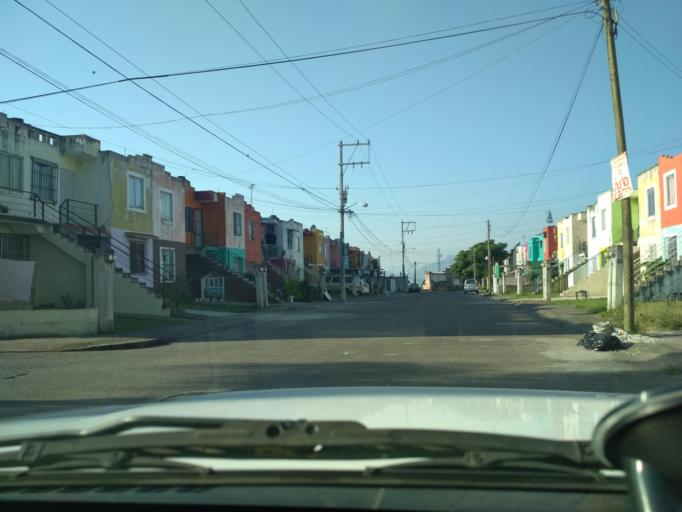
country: MX
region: Veracruz
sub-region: Fortin
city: Fraccionamiento Villas de la Llave
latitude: 18.9183
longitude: -96.9940
